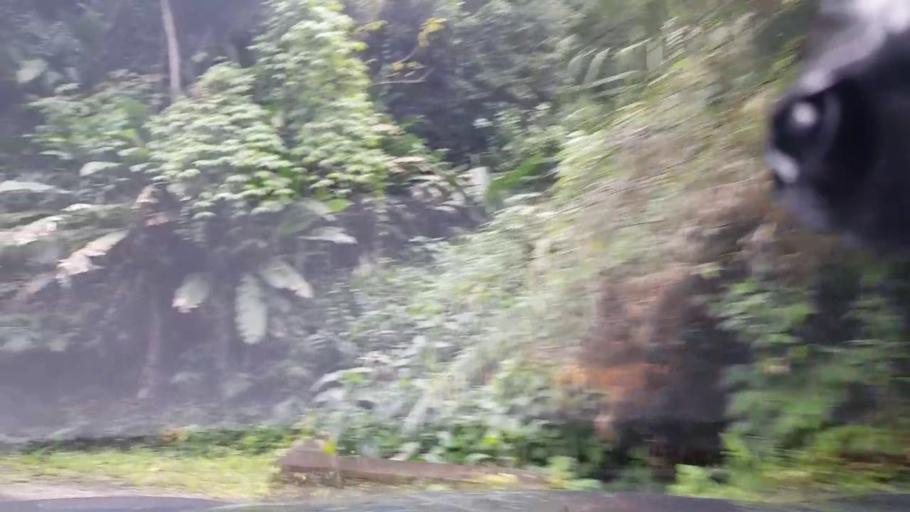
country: JM
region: Saint Andrew
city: Gordon Town
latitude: 18.1052
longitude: -76.7172
